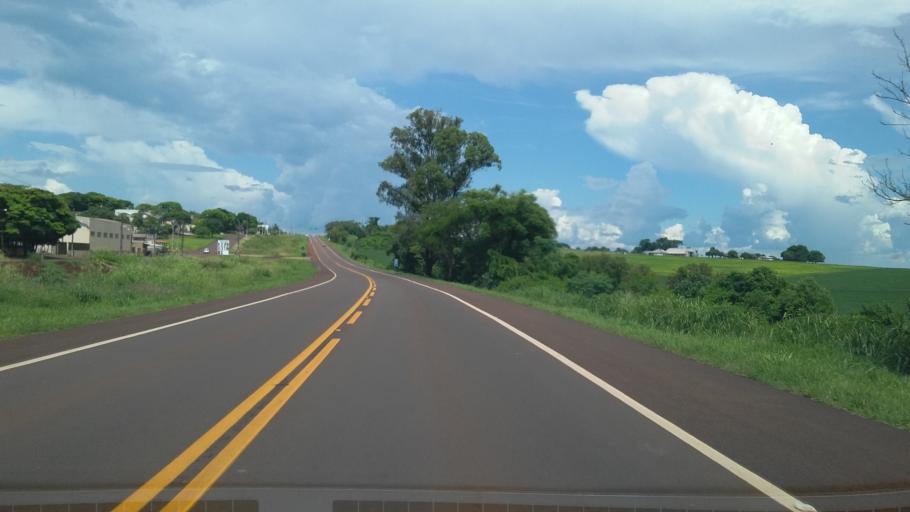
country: BR
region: Parana
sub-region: Corbelia
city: Corbelia
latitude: -24.5577
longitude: -52.9923
